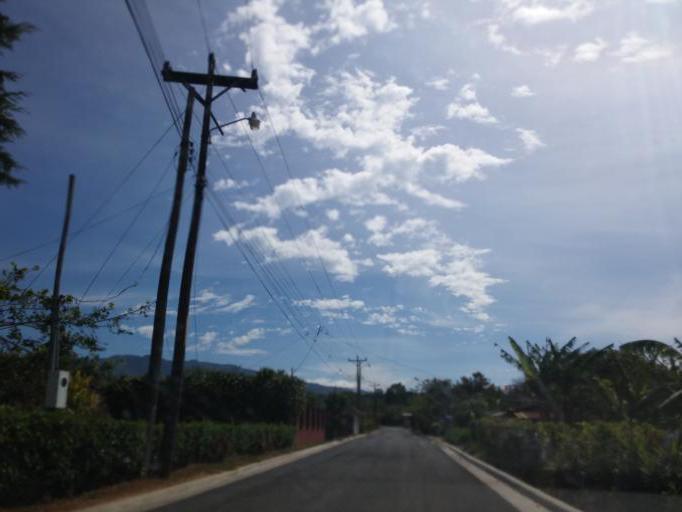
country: CR
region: Alajuela
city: Sabanilla
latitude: 10.0720
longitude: -84.2049
